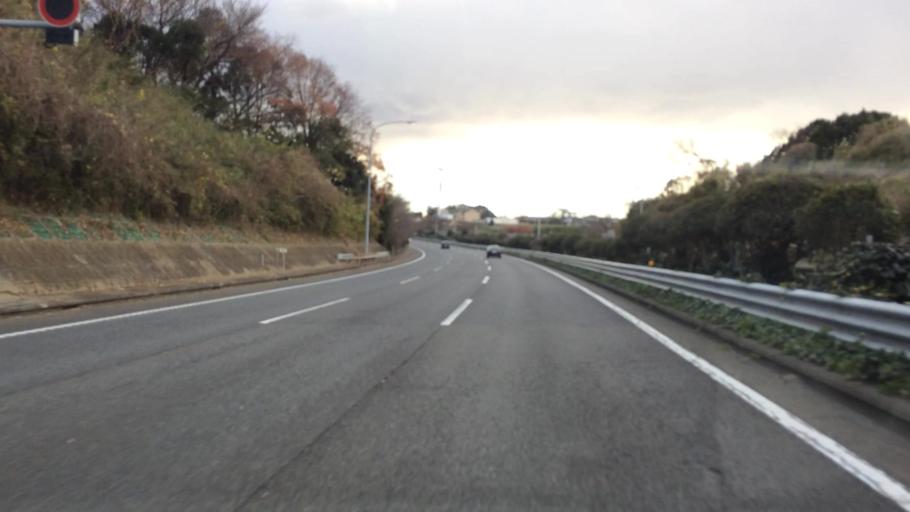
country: JP
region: Kanagawa
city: Yokohama
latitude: 35.4987
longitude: 139.5914
